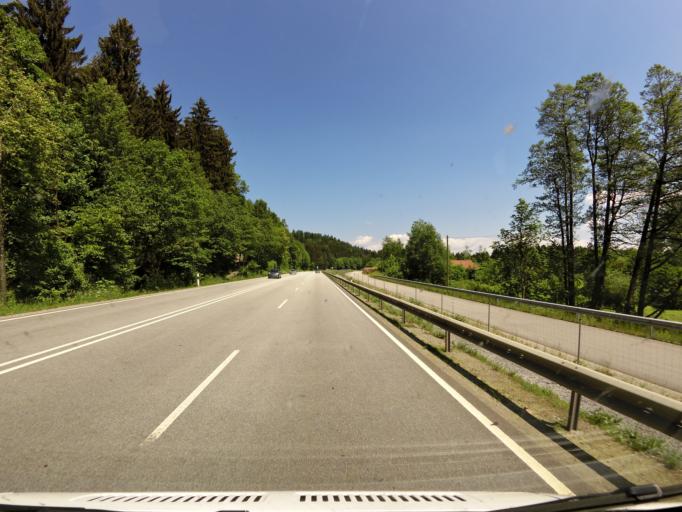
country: DE
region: Bavaria
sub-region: Lower Bavaria
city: Buchlberg
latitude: 48.6825
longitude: 13.4901
